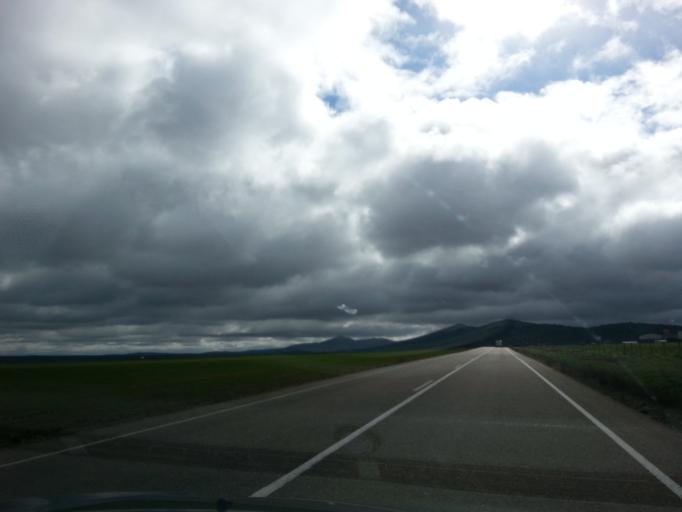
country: ES
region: Castille and Leon
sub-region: Provincia de Salamanca
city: Tamames
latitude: 40.6677
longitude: -6.1171
